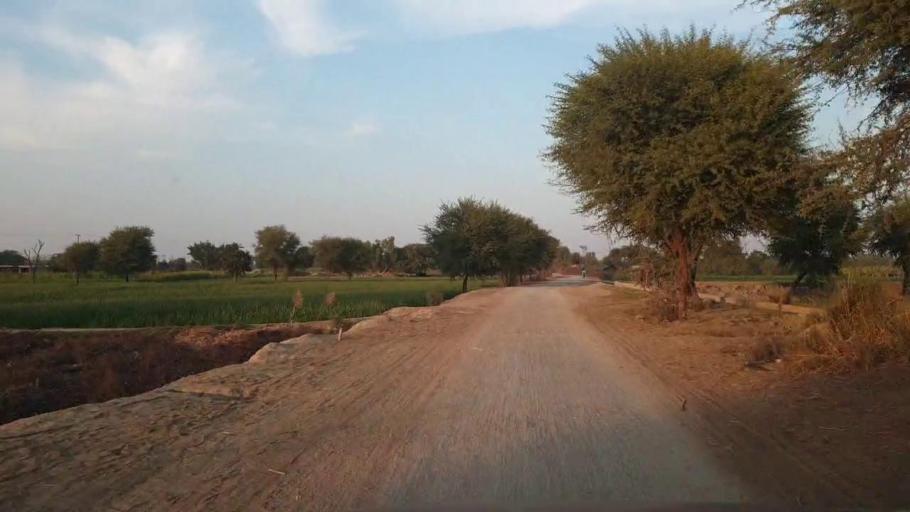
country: PK
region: Sindh
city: Shahpur Chakar
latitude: 26.1974
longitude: 68.6188
